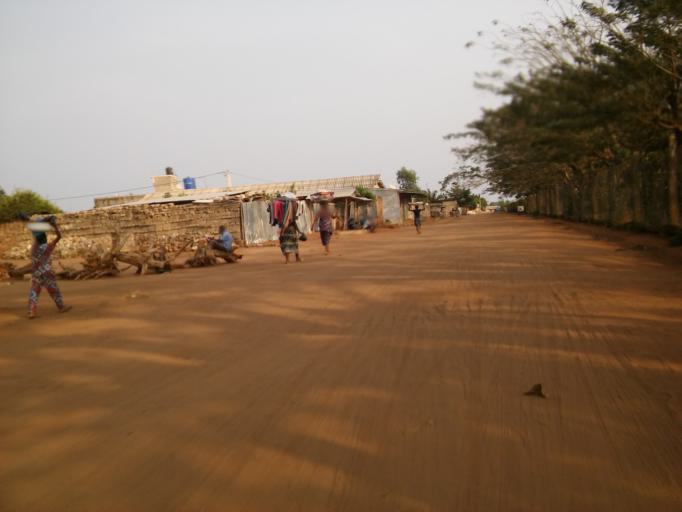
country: BJ
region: Atlantique
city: Abomey-Calavi
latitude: 6.4203
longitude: 2.3321
